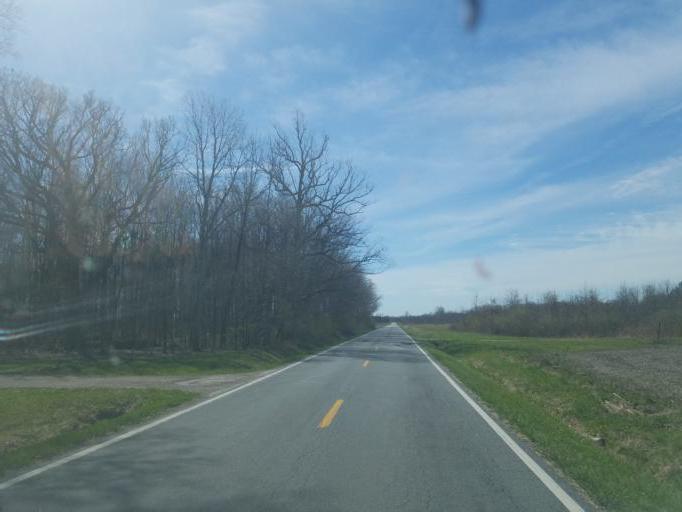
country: US
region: Ohio
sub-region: Delaware County
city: Ashley
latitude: 40.3950
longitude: -83.0384
